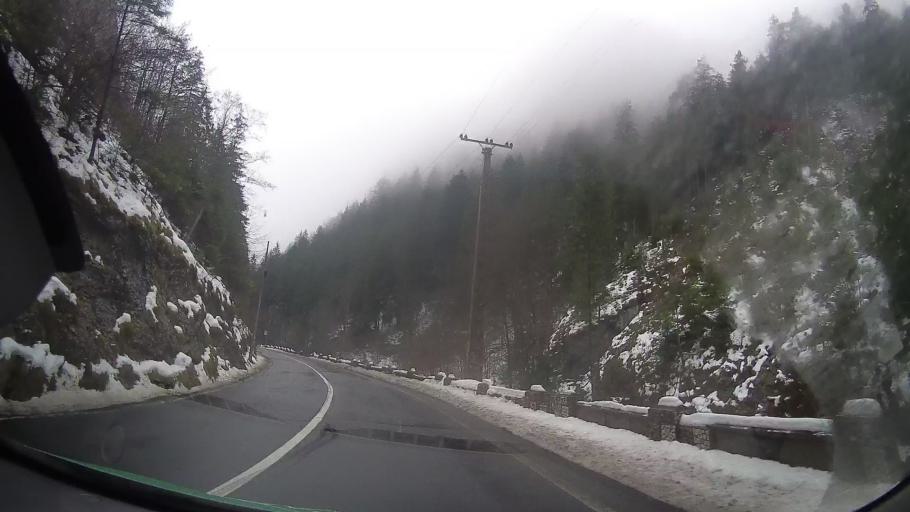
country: RO
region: Neamt
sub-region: Comuna Bicaz Chei
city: Bicaz Chei
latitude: 46.8013
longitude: 25.8011
